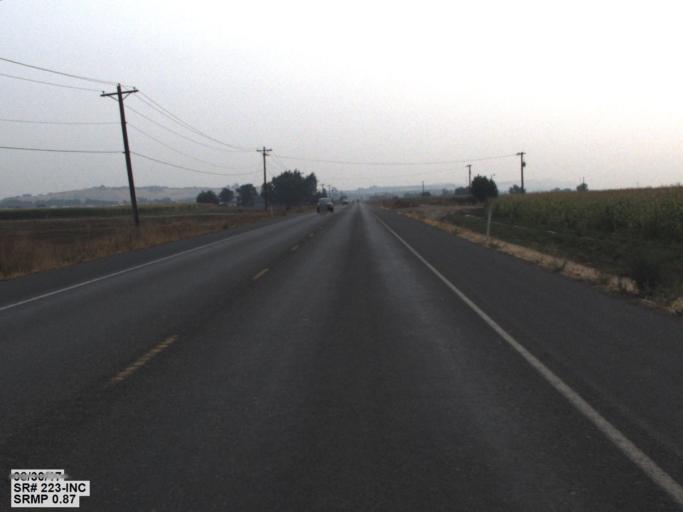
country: US
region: Washington
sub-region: Yakima County
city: Granger
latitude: 46.3284
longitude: -120.2280
